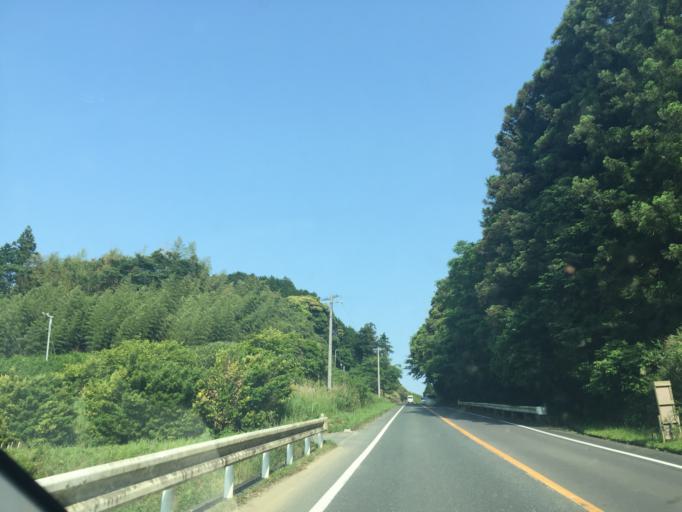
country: JP
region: Shizuoka
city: Kakegawa
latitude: 34.7947
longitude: 138.0013
